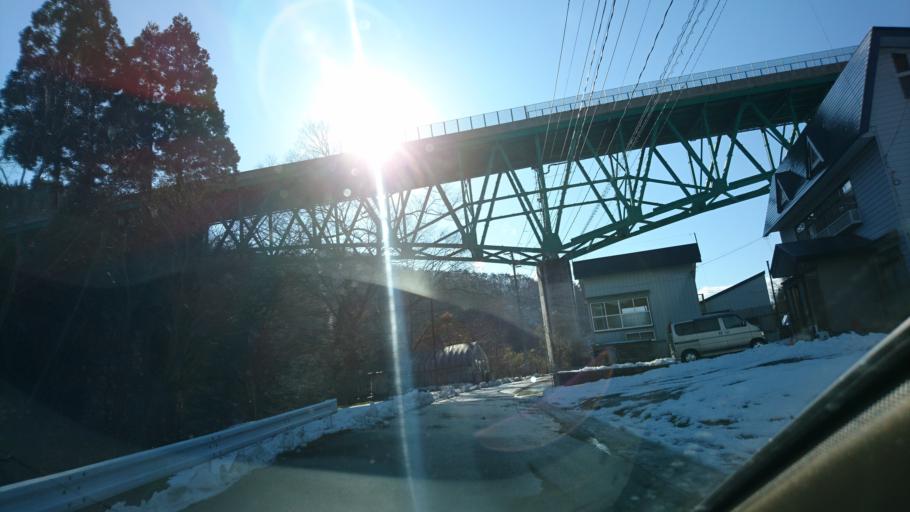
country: JP
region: Akita
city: Yokotemachi
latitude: 39.3127
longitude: 140.7740
